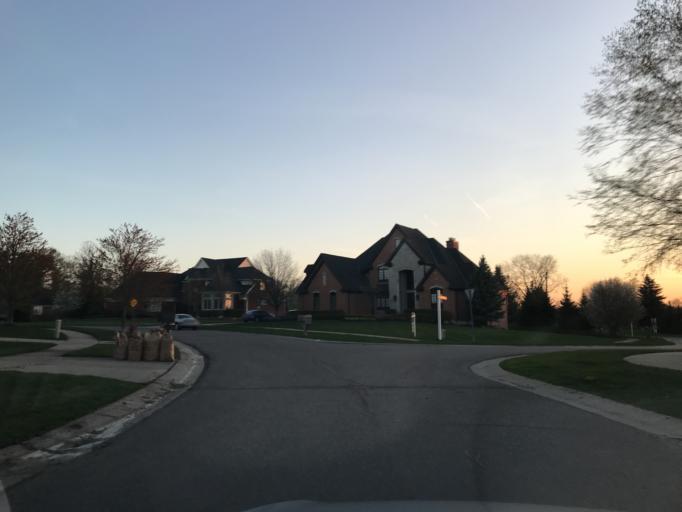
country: US
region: Michigan
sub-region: Oakland County
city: South Lyon
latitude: 42.4600
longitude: -83.5911
